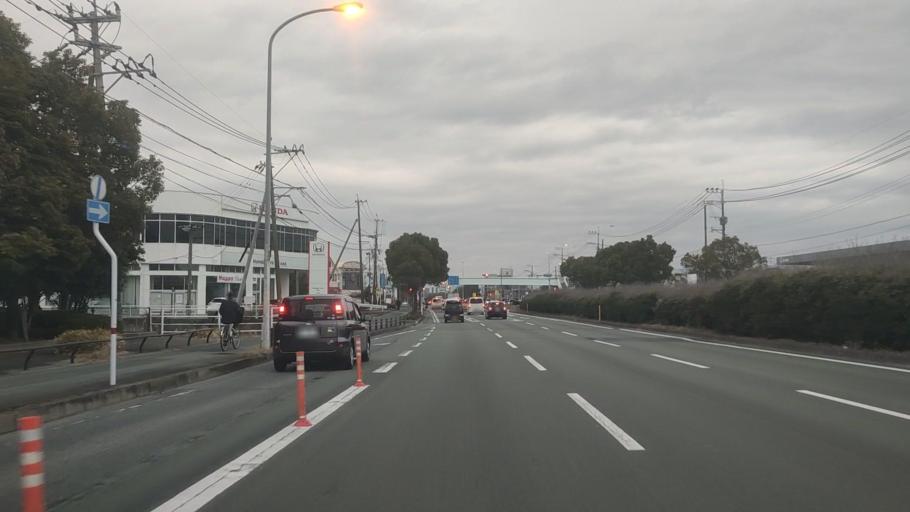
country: JP
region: Kumamoto
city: Kumamoto
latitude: 32.7695
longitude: 130.7283
